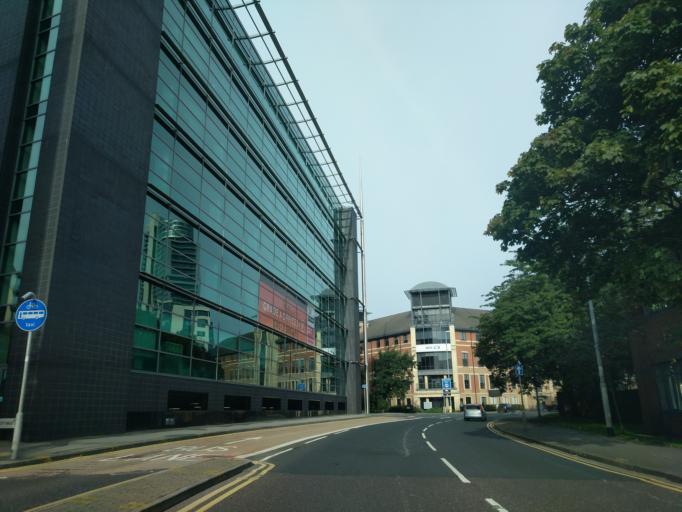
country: GB
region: England
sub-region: City and Borough of Leeds
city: Leeds
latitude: 53.7895
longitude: -1.5464
